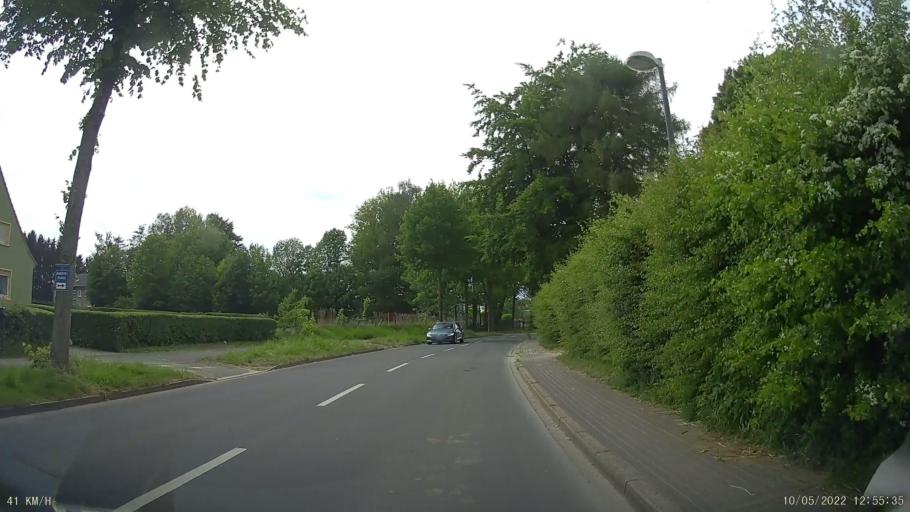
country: DE
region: North Rhine-Westphalia
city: Castrop-Rauxel
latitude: 51.5266
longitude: 7.3325
